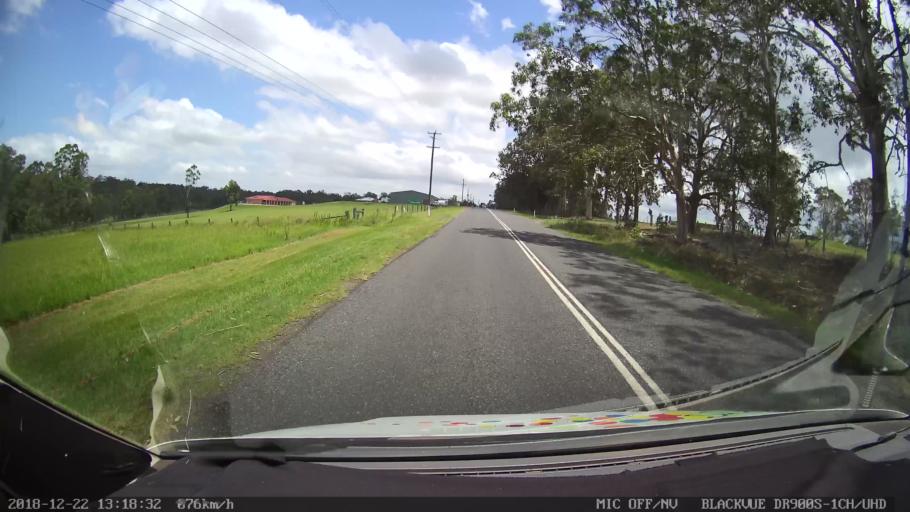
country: AU
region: New South Wales
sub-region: Clarence Valley
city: South Grafton
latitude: -29.7478
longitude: 152.9340
